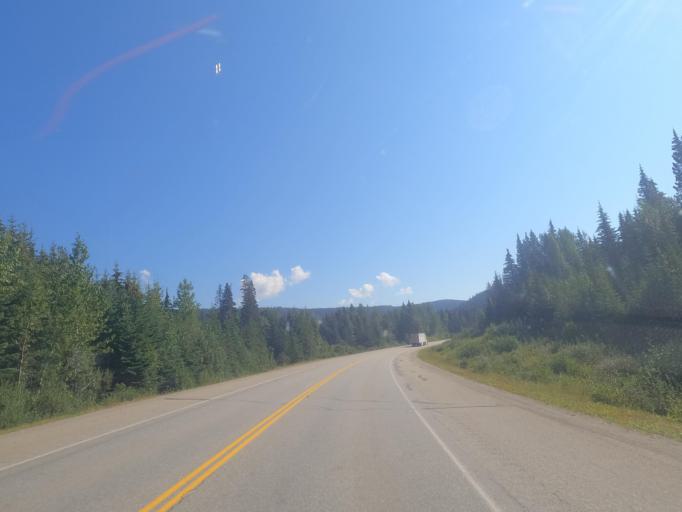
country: CA
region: Alberta
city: Jasper Park Lodge
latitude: 52.8878
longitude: -118.4790
